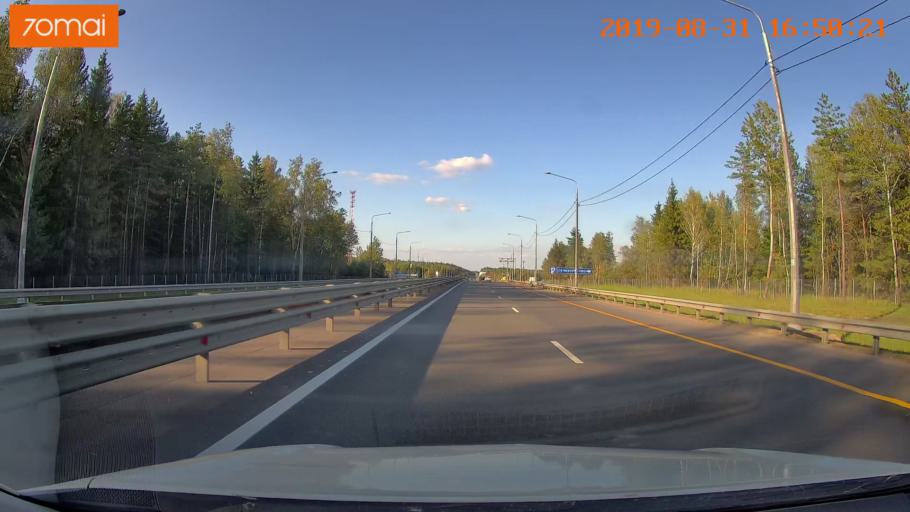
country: RU
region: Kaluga
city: Pyatovskiy
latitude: 54.7071
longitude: 36.1619
